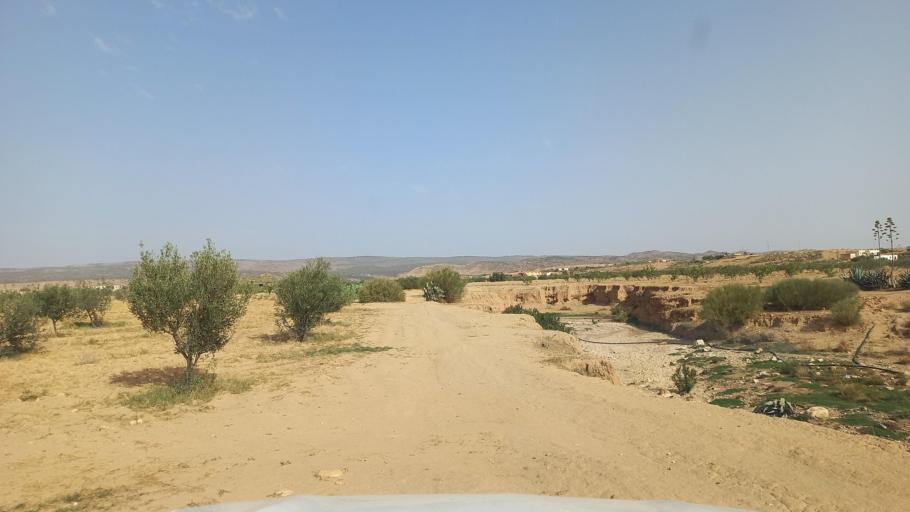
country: TN
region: Al Qasrayn
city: Kasserine
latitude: 35.2955
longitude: 8.9674
